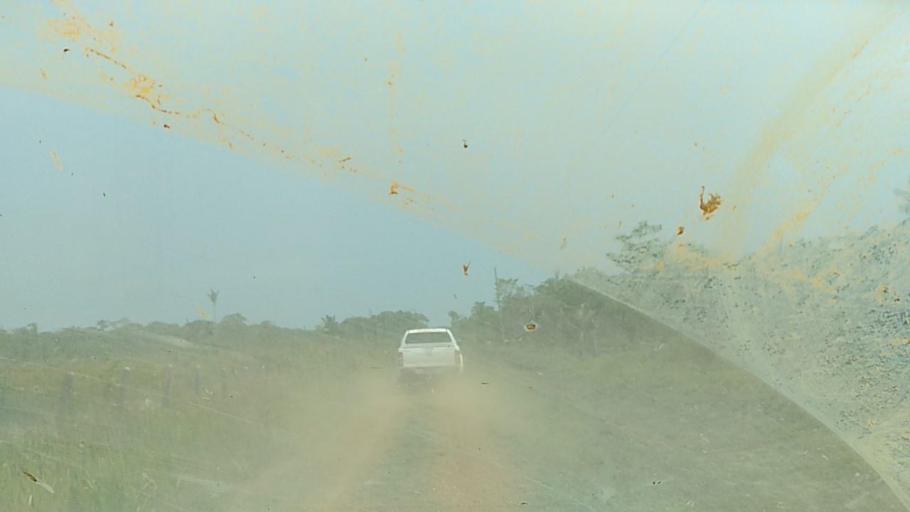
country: BR
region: Rondonia
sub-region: Porto Velho
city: Porto Velho
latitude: -8.9711
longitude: -64.3888
